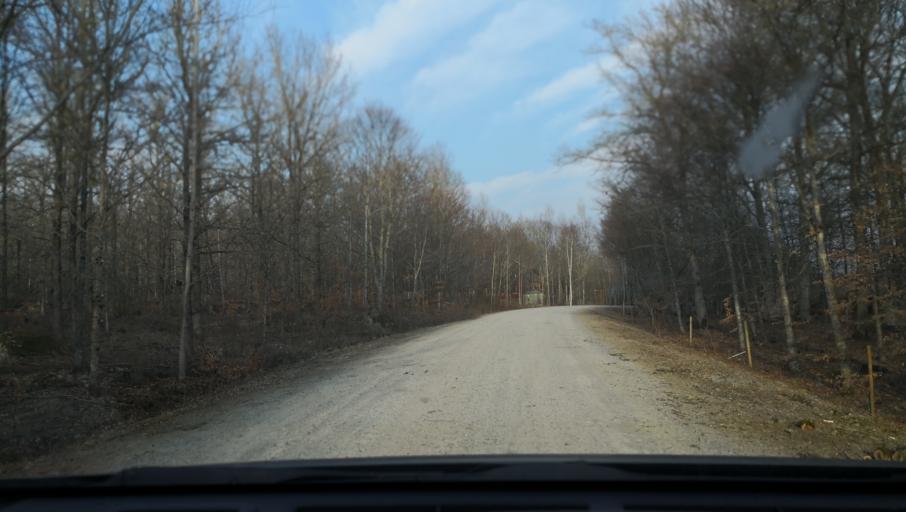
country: SE
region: OErebro
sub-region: Orebro Kommun
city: Hovsta
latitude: 59.3891
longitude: 15.2614
